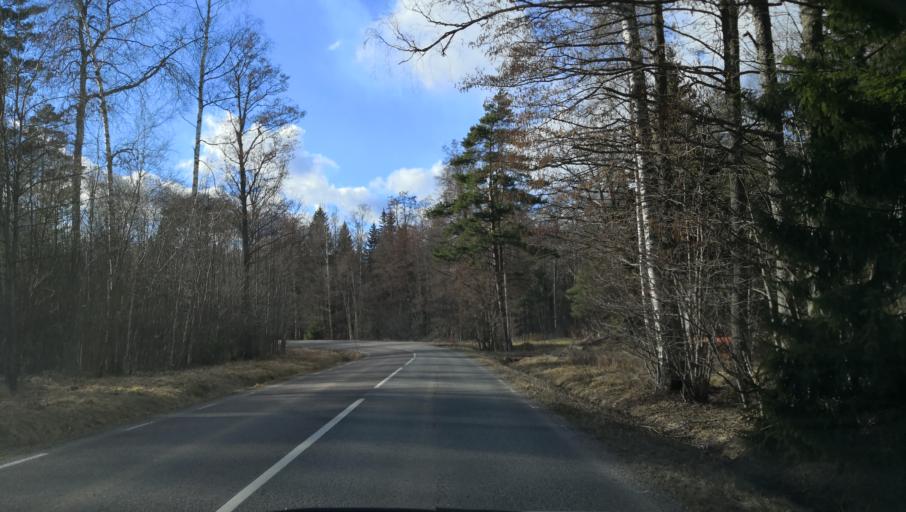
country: SE
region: Stockholm
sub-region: Varmdo Kommun
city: Hemmesta
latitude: 59.2868
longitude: 18.4779
